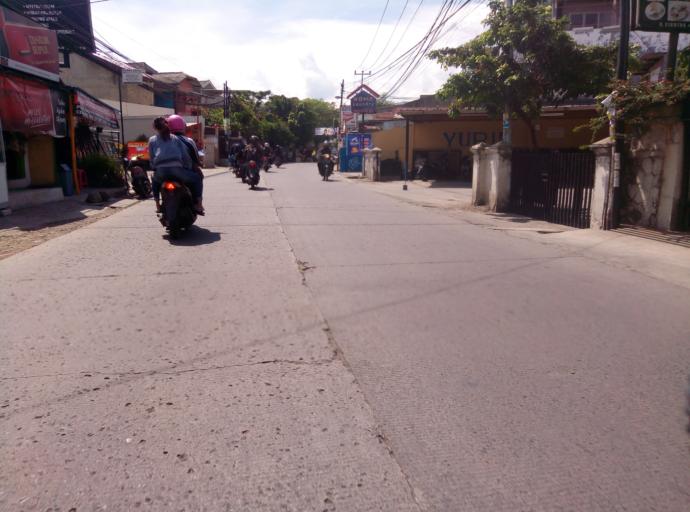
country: ID
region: West Java
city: Bandung
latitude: -6.8993
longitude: 107.6435
